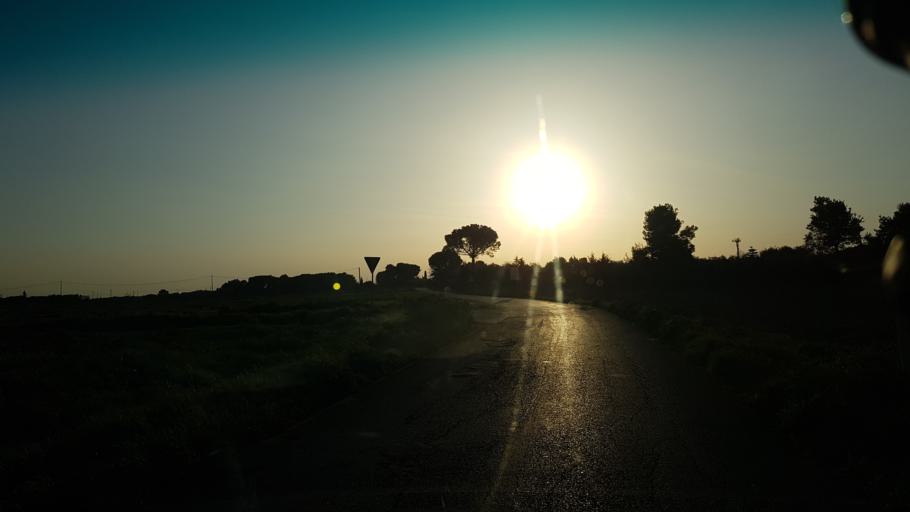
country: IT
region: Apulia
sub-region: Provincia di Brindisi
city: Mesagne
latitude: 40.5533
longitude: 17.8020
